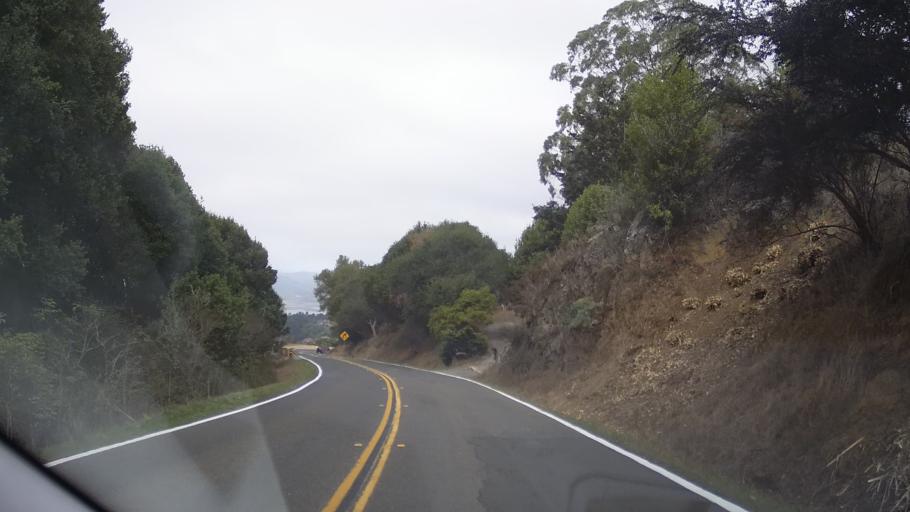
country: US
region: California
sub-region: Marin County
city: Bolinas
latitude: 37.8952
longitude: -122.6302
